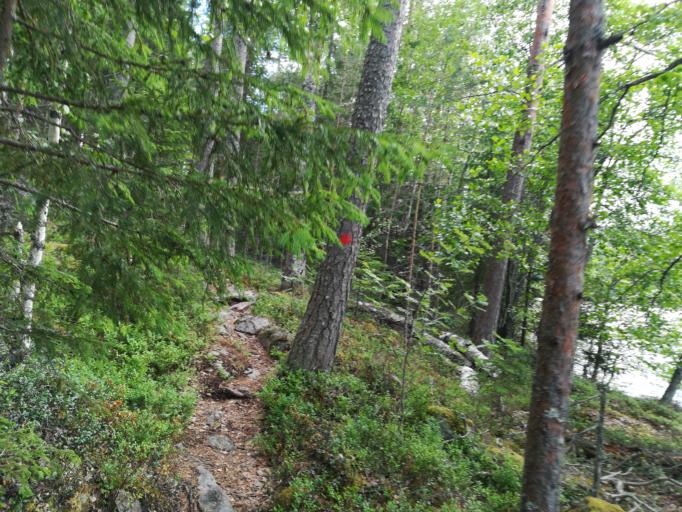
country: FI
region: South Karelia
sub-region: Lappeenranta
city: Savitaipale
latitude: 61.3043
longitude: 27.6123
